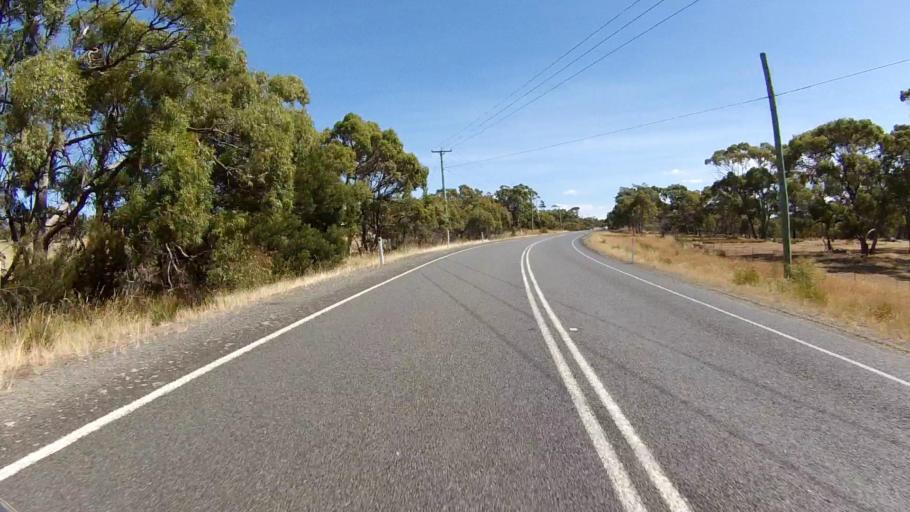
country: AU
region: Tasmania
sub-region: Sorell
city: Sorell
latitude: -42.5808
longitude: 147.8145
